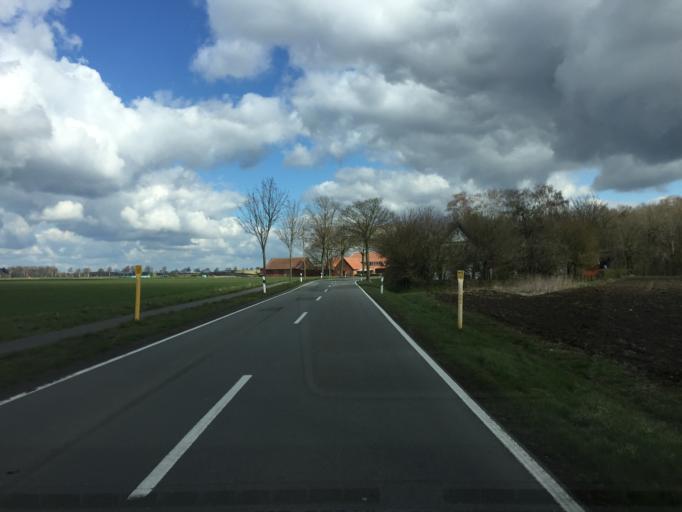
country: DE
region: Lower Saxony
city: Sudwalde
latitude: 52.7669
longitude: 8.8510
